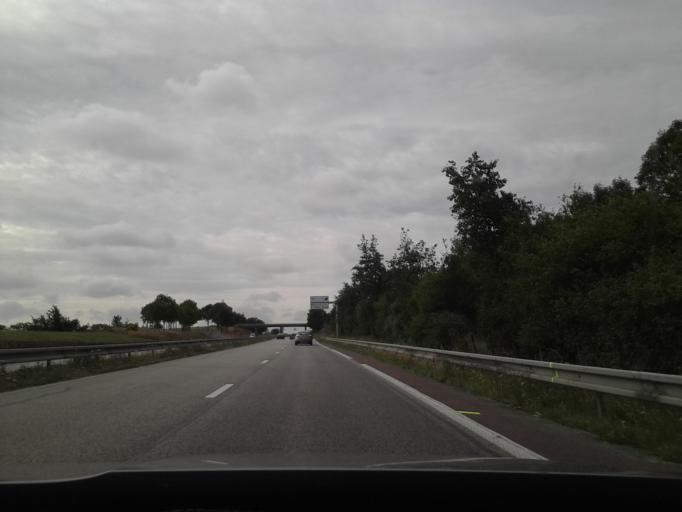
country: FR
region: Lower Normandy
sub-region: Departement de la Manche
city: Sainte-Mere-Eglise
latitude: 49.4277
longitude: -1.3325
